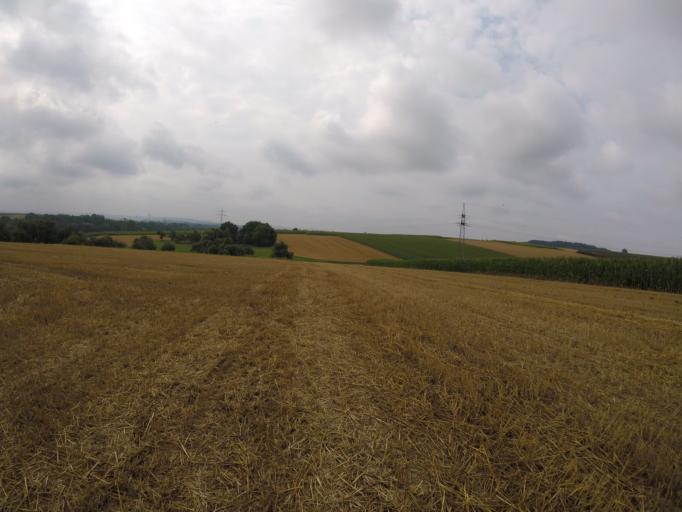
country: DE
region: Baden-Wuerttemberg
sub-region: Regierungsbezirk Stuttgart
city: Aspach
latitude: 48.9605
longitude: 9.3903
